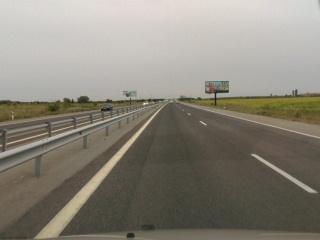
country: BG
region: Stara Zagora
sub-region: Obshtina Stara Zagora
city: Stara Zagora
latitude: 42.3202
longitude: 25.5644
